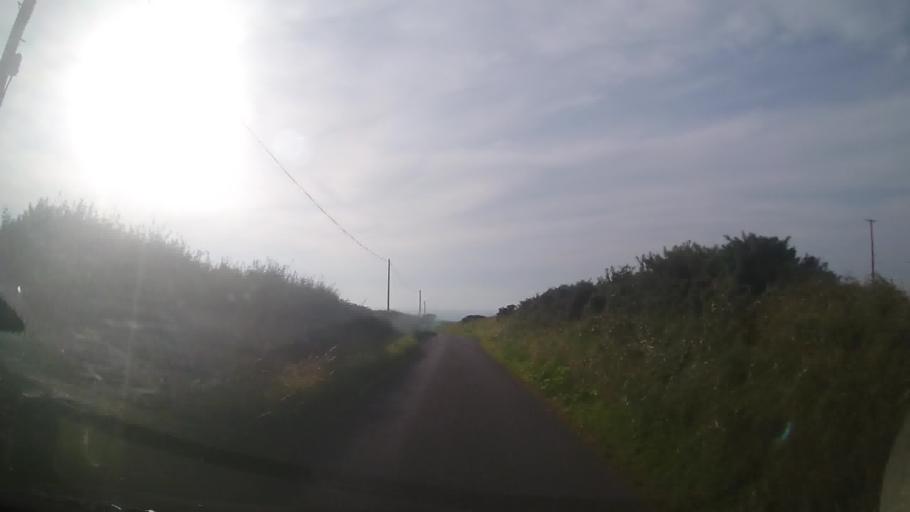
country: GB
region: Wales
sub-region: Pembrokeshire
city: Llanrhian
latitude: 51.9290
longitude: -5.1875
